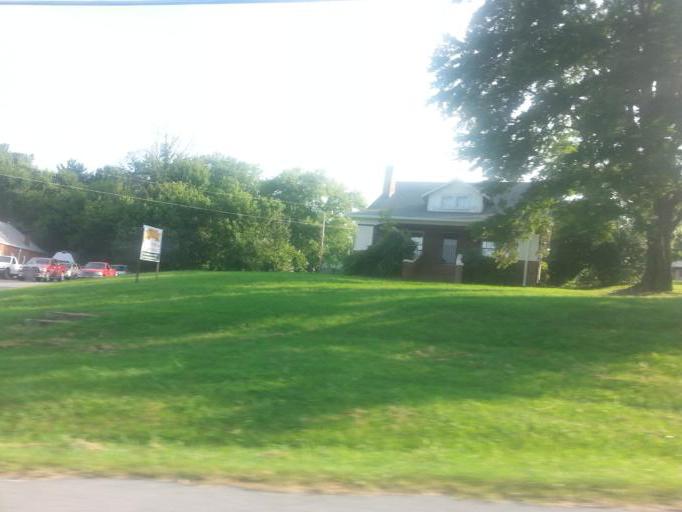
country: US
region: Tennessee
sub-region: Sevier County
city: Sevierville
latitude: 35.8723
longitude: -83.5764
